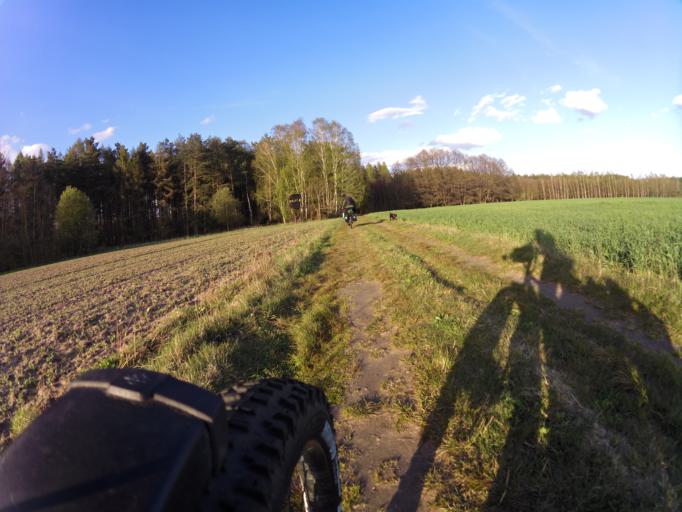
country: PL
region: West Pomeranian Voivodeship
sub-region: Powiat gryficki
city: Ploty
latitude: 53.7515
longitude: 15.2833
